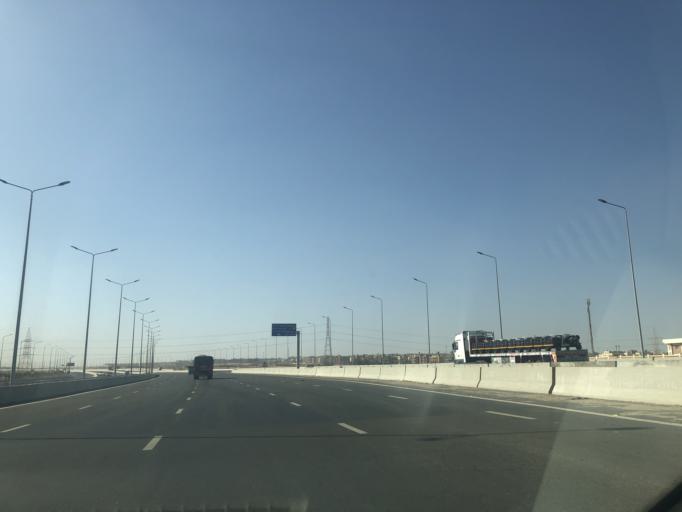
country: EG
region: Al Jizah
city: Madinat Sittah Uktubar
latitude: 29.9629
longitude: 30.8894
